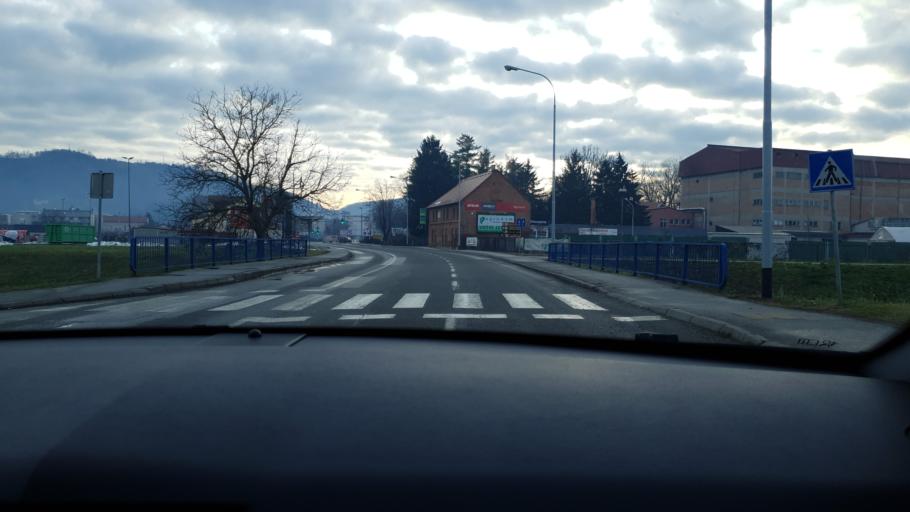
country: HR
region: Pozesko-Slavonska
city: Pozega
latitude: 45.3410
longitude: 17.6827
